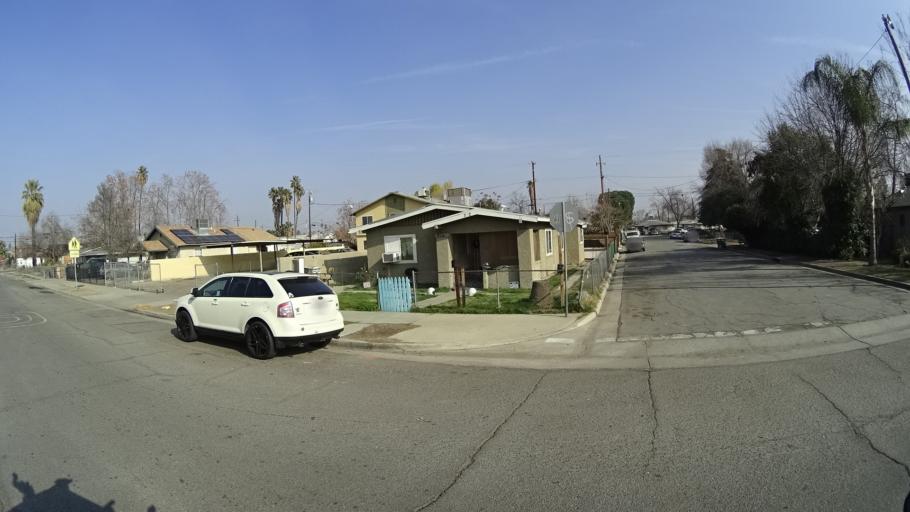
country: US
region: California
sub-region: Kern County
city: Bakersfield
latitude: 35.3636
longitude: -119.0142
